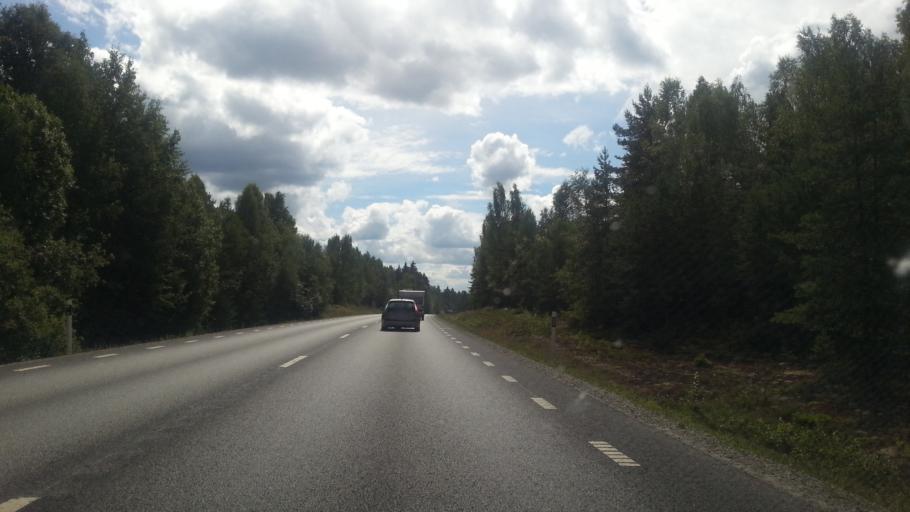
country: SE
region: OErebro
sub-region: Lindesbergs Kommun
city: Lindesberg
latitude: 59.5614
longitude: 15.2190
